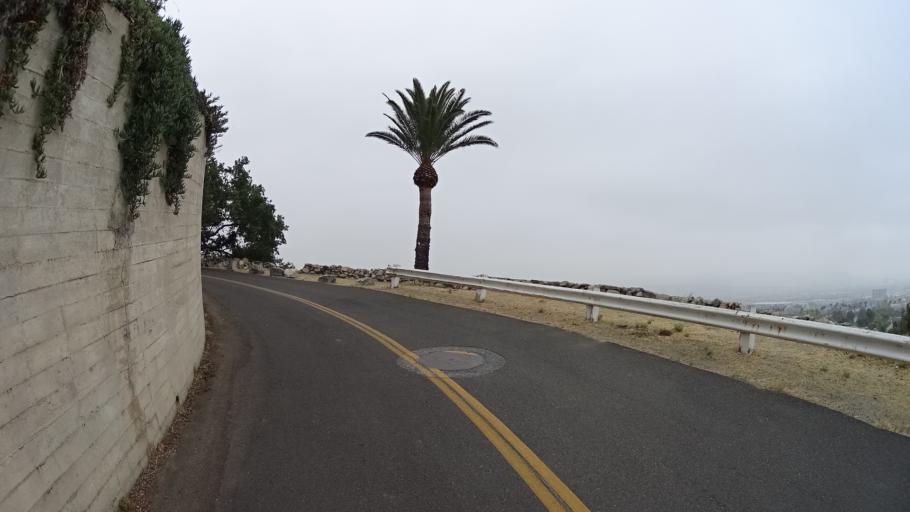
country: US
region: California
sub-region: Los Angeles County
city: Burbank
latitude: 34.1928
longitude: -118.2947
